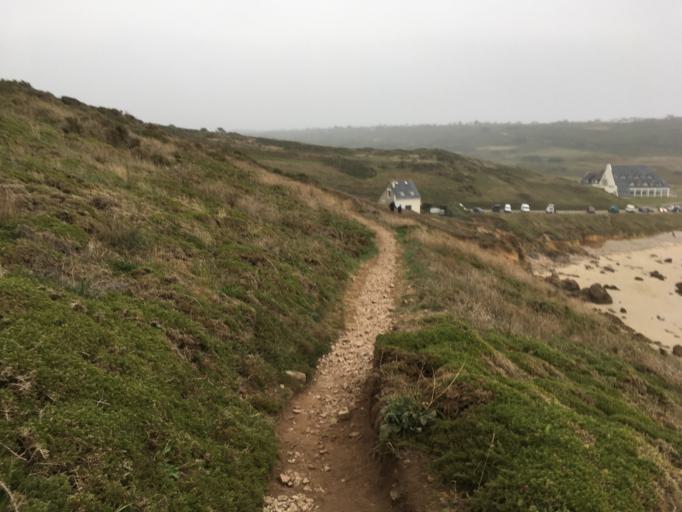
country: FR
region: Brittany
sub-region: Departement du Finistere
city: Plogoff
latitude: 48.0503
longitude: -4.7068
